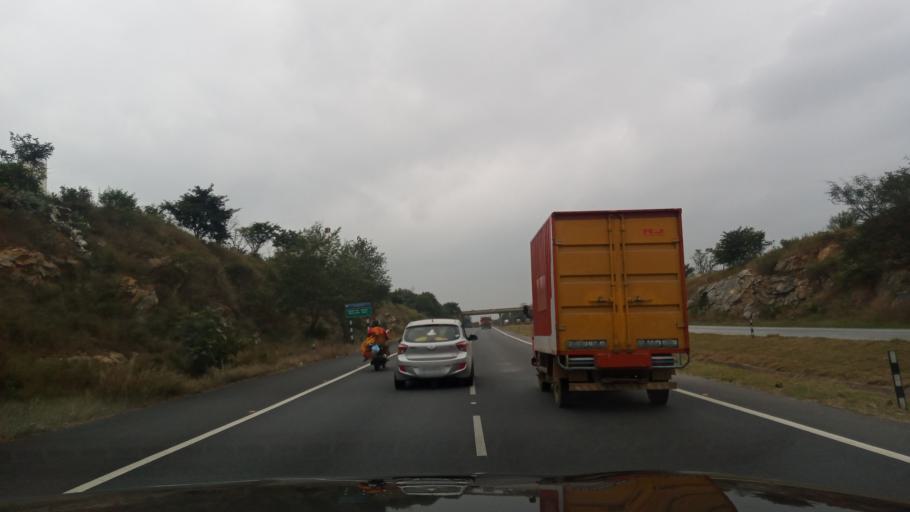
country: IN
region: Karnataka
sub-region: Bangalore Rural
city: Nelamangala
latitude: 13.0122
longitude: 77.4757
